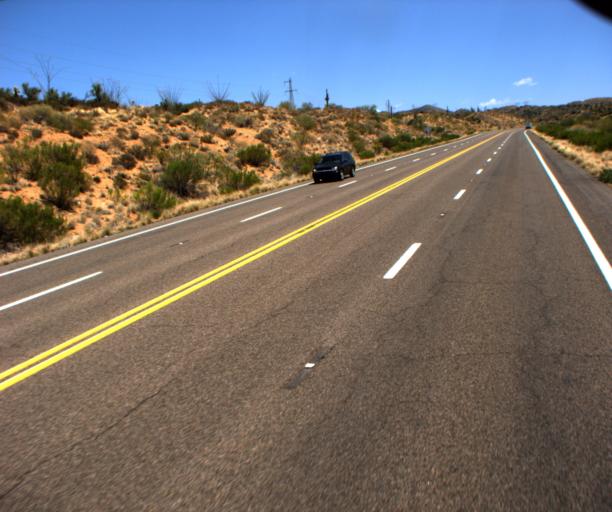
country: US
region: Arizona
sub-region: Gila County
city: Miami
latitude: 33.5745
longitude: -110.9570
